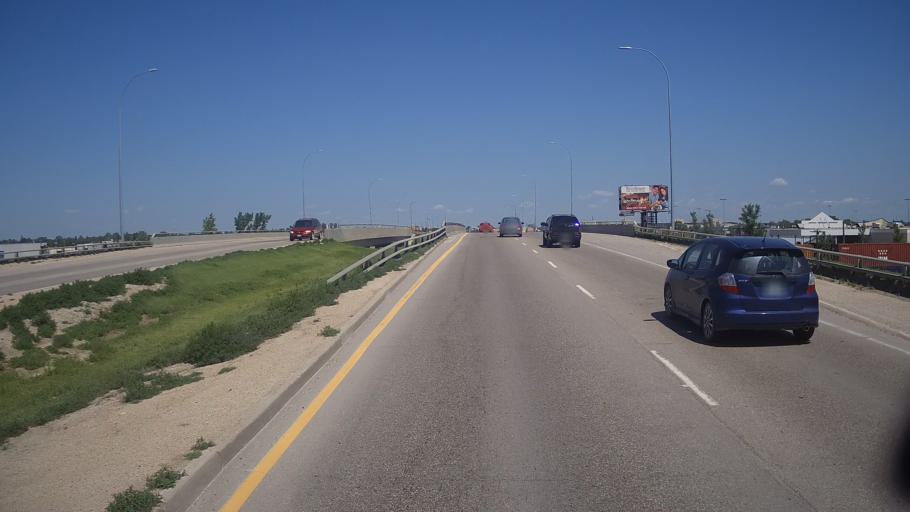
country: CA
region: Manitoba
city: Winnipeg
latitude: 49.8932
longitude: -97.0711
